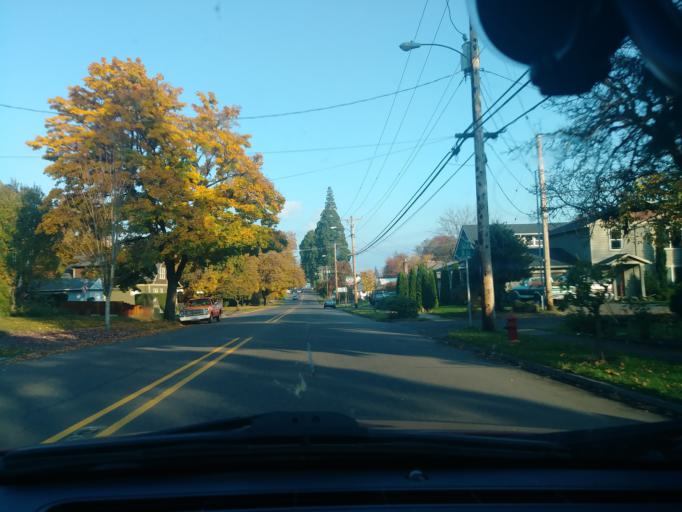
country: US
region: Oregon
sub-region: Washington County
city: Forest Grove
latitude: 45.5196
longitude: -123.1190
